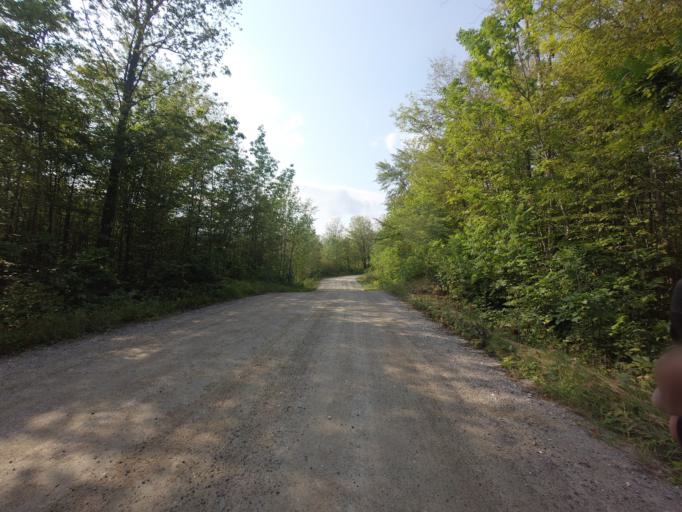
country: CA
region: Ontario
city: Perth
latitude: 44.8231
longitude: -76.7130
